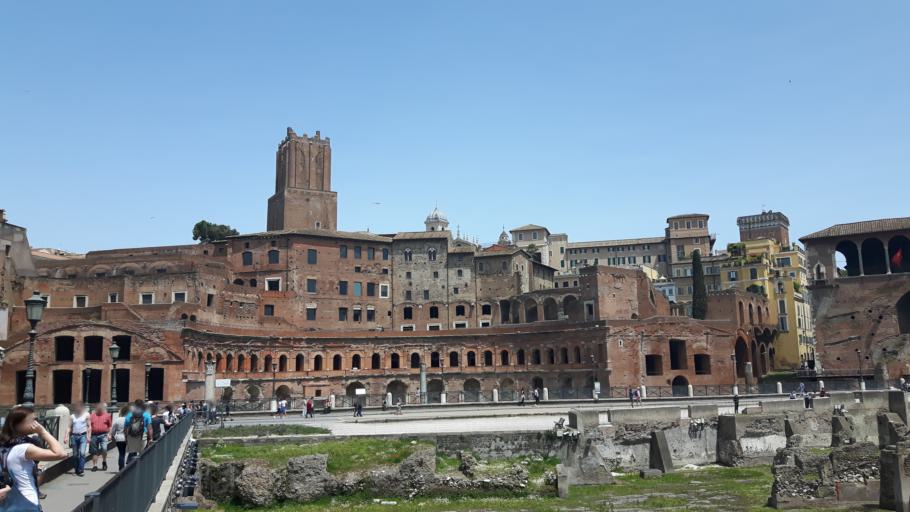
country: IT
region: Latium
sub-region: Citta metropolitana di Roma Capitale
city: Rome
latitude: 41.8949
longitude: 12.4848
